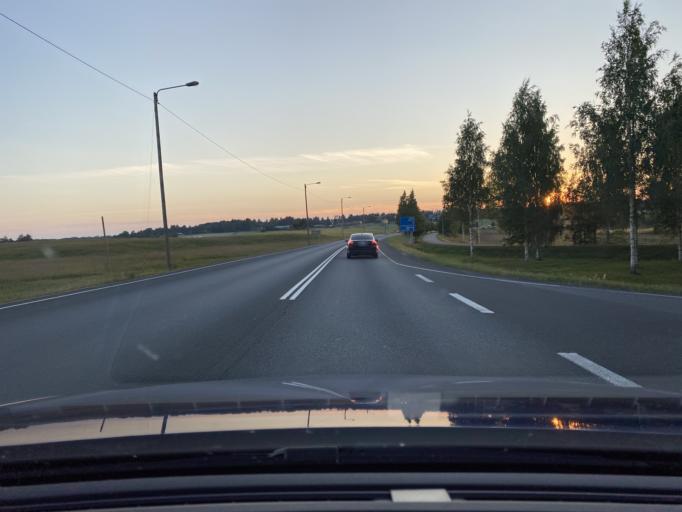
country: FI
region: Pirkanmaa
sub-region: Luoteis-Pirkanmaa
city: Ikaalinen
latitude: 61.7574
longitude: 23.0336
